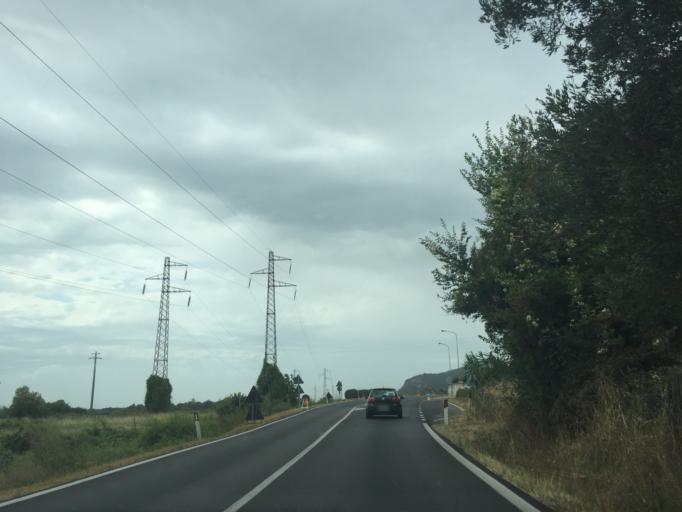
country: IT
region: Tuscany
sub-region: Province of Pisa
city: Gabella
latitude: 43.7318
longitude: 10.4804
